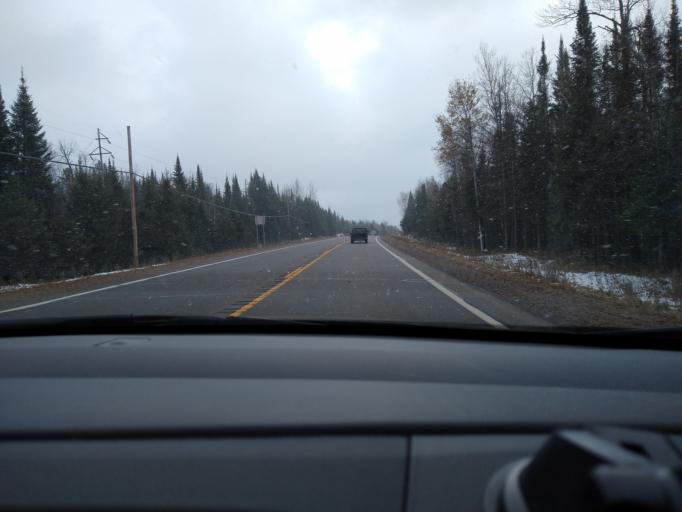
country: US
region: Michigan
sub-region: Dickinson County
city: Iron Mountain
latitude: 46.0337
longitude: -88.0598
